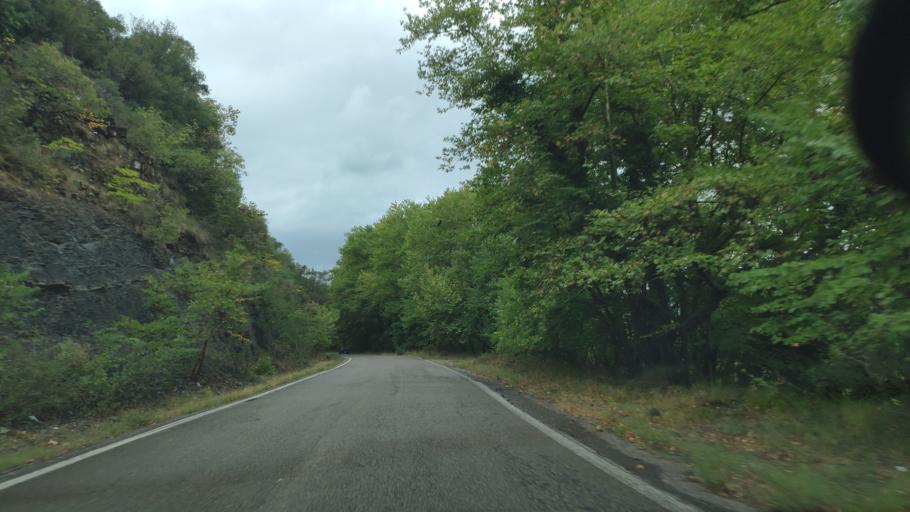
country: GR
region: West Greece
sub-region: Nomos Aitolias kai Akarnanias
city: Krikellos
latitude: 38.9583
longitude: 21.3372
